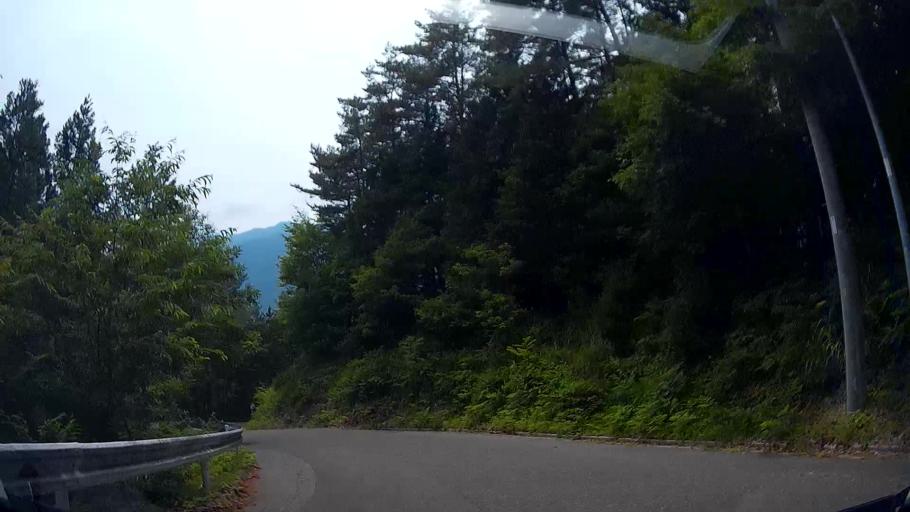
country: JP
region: Nagano
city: Iida
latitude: 35.2836
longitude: 137.9234
